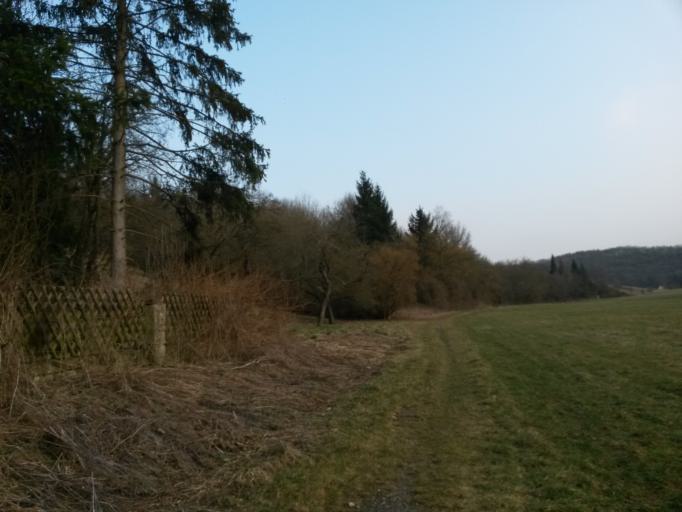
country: DE
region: Bavaria
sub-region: Regierungsbezirk Unterfranken
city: Rimpar
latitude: 49.8421
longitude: 9.9588
